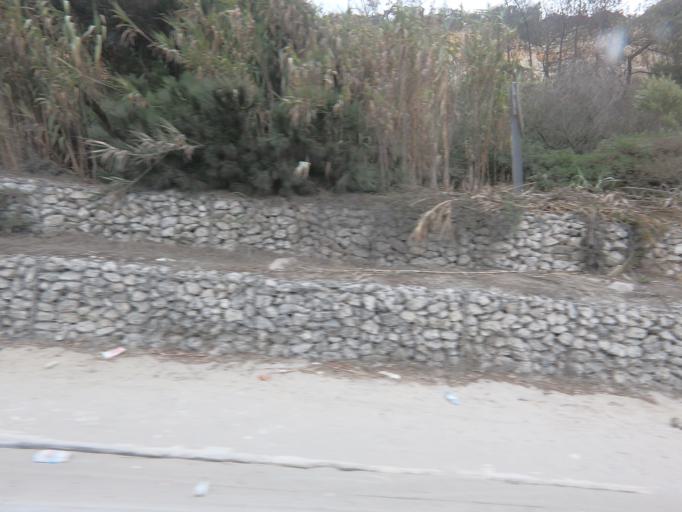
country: PT
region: Setubal
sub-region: Almada
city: Charneca
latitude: 38.5735
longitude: -9.1940
